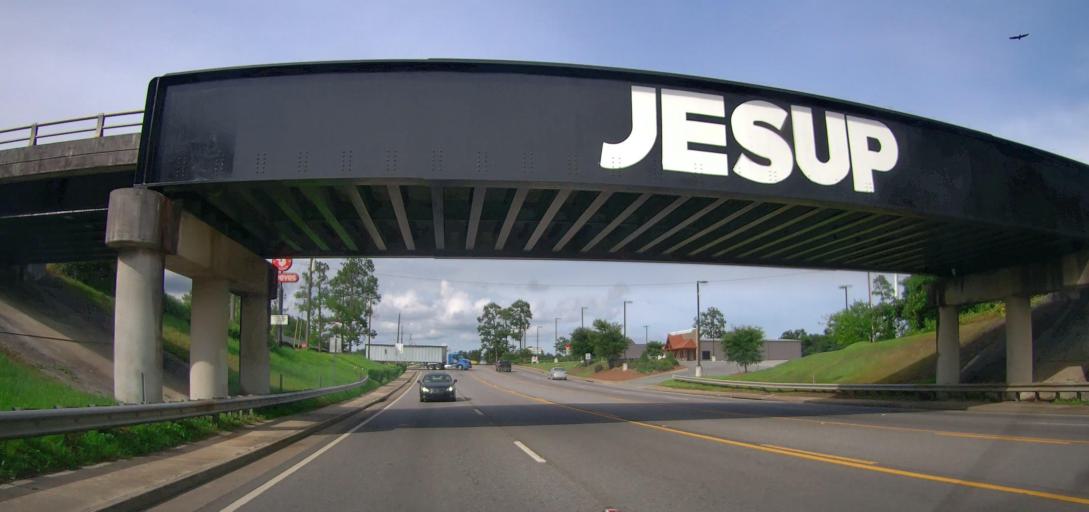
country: US
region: Georgia
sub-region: Wayne County
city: Jesup
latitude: 31.6107
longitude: -81.8816
